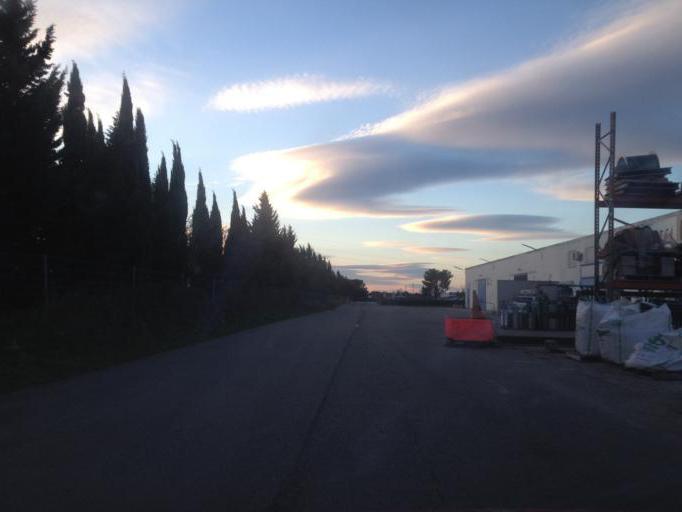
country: FR
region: Provence-Alpes-Cote d'Azur
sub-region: Departement du Vaucluse
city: Orange
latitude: 44.1108
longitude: 4.8390
